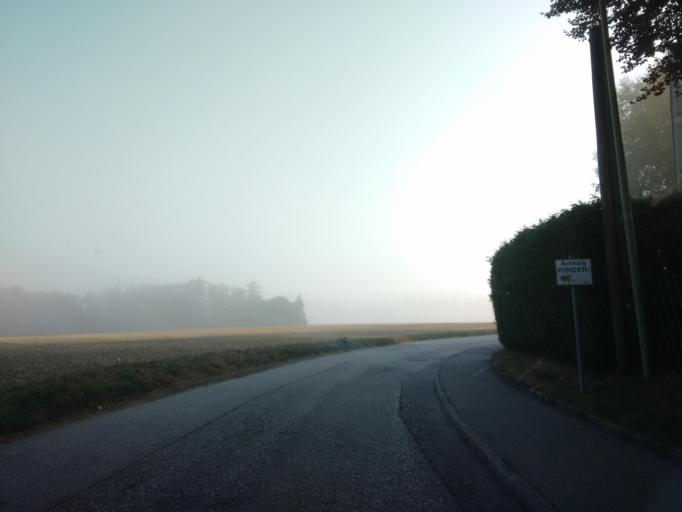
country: AT
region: Upper Austria
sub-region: Wels-Land
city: Buchkirchen
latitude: 48.1918
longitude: 14.0004
